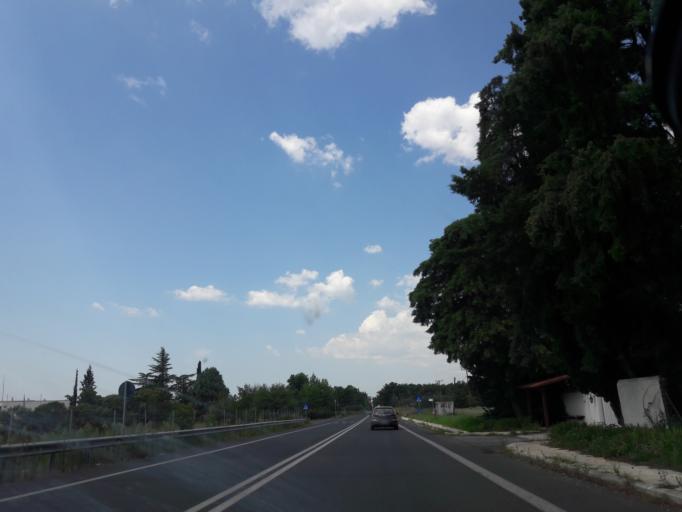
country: GR
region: Central Macedonia
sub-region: Nomos Thessalonikis
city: Souroti
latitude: 40.5104
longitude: 23.0816
